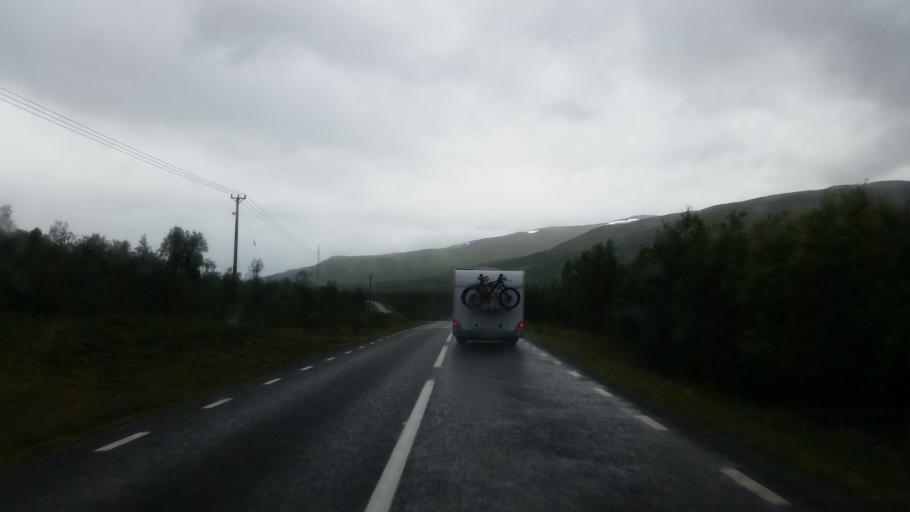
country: NO
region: Nordland
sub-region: Rana
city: Mo i Rana
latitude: 65.9176
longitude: 14.9974
